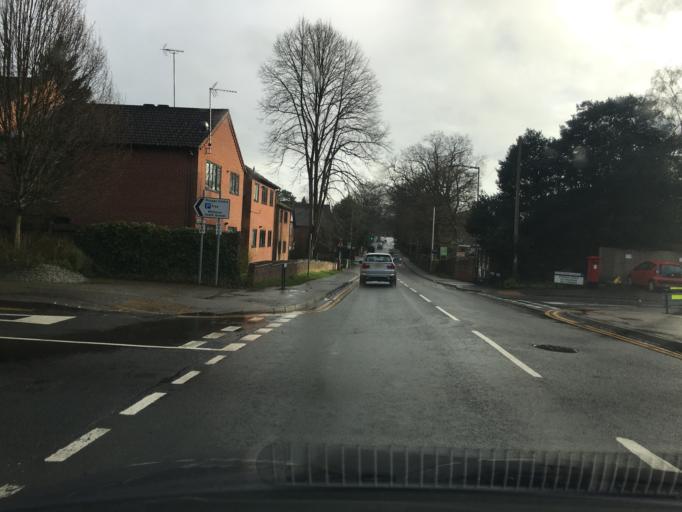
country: GB
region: England
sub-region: Bracknell Forest
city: Crowthorne
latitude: 51.3665
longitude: -0.7948
